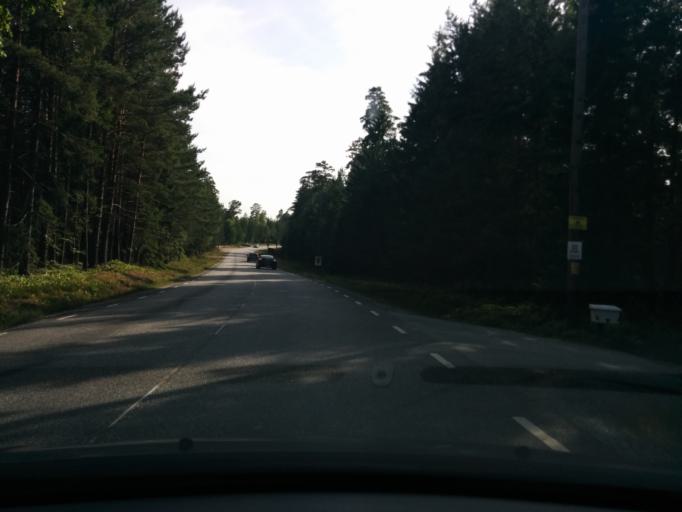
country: SE
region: Stockholm
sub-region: Varmdo Kommun
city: Holo
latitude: 59.3063
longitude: 18.6817
